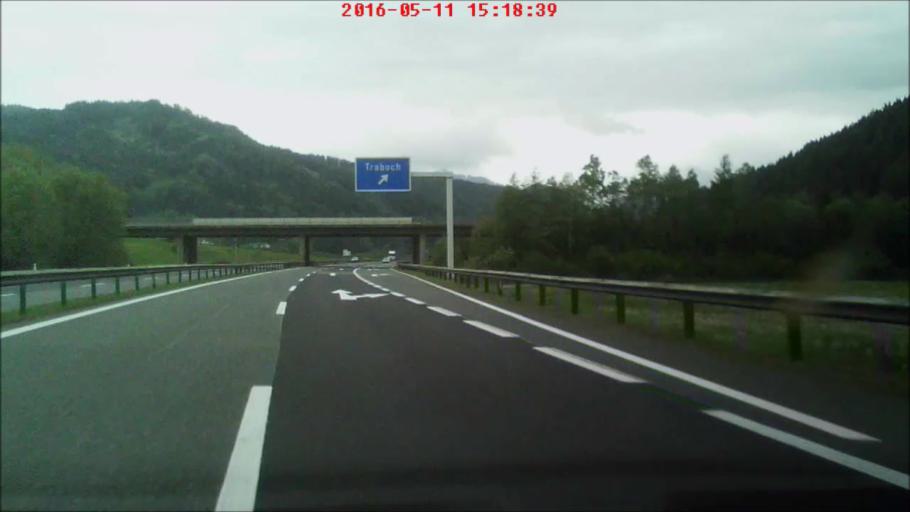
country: AT
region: Styria
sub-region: Politischer Bezirk Leoben
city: Traboch
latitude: 47.3711
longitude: 14.9887
